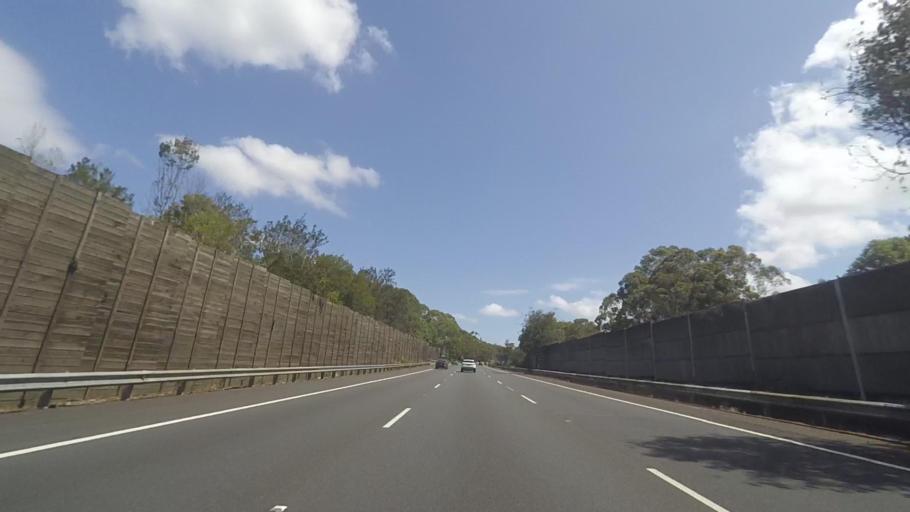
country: AU
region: New South Wales
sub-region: Ku-ring-gai
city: North Wahroonga
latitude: -33.7028
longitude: 151.1182
